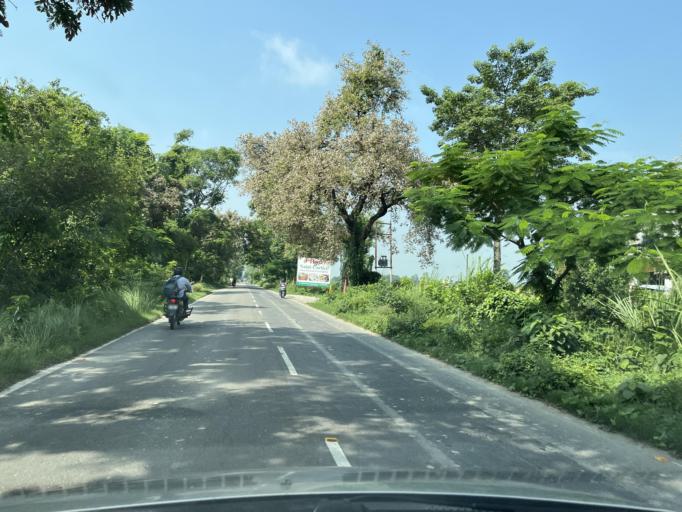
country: IN
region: Uttarakhand
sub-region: Udham Singh Nagar
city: Bazpur
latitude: 29.1892
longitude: 79.1892
